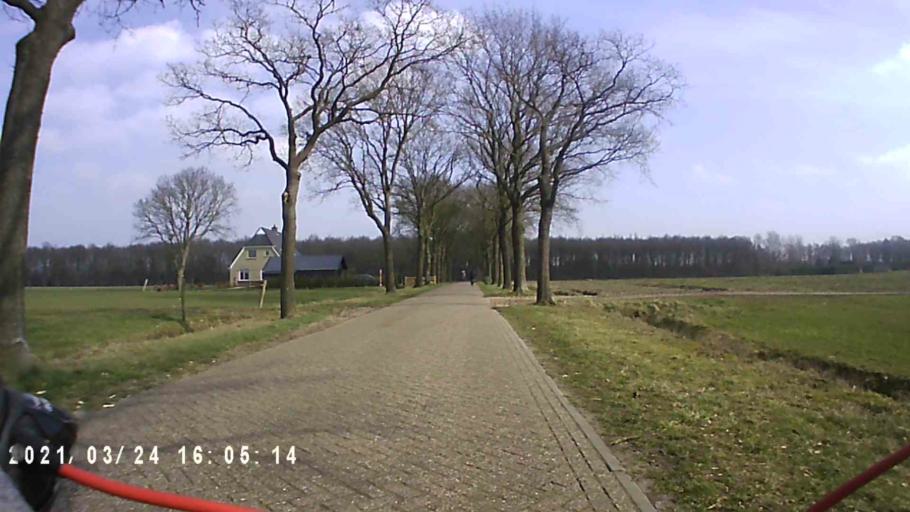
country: NL
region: Friesland
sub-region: Gemeente Heerenveen
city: Jubbega
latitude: 53.0316
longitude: 6.2144
